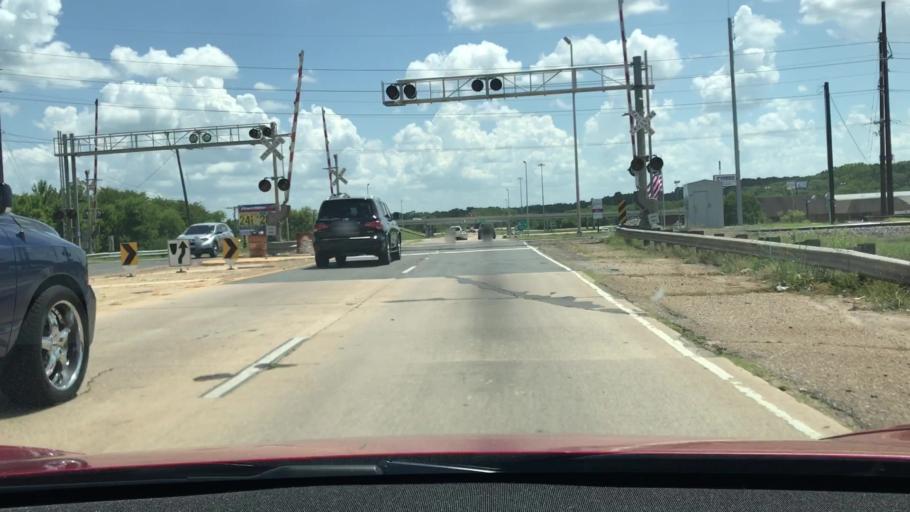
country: US
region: Louisiana
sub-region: Bossier Parish
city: Bossier City
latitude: 32.4153
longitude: -93.7234
